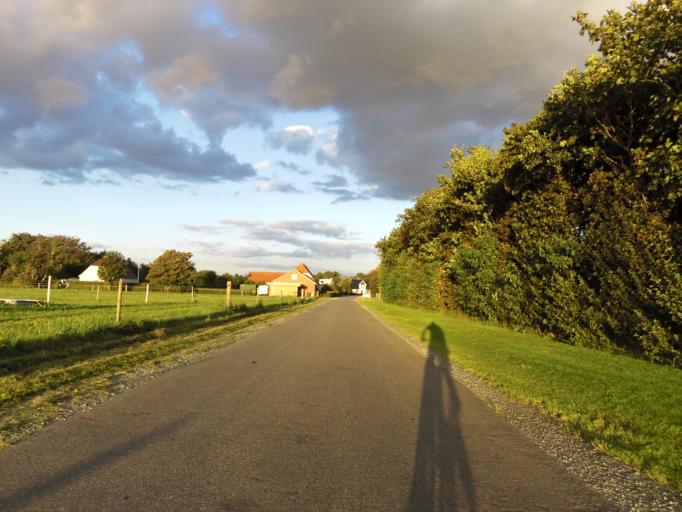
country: DK
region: South Denmark
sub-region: Tonder Kommune
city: Sherrebek
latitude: 55.2387
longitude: 8.8420
